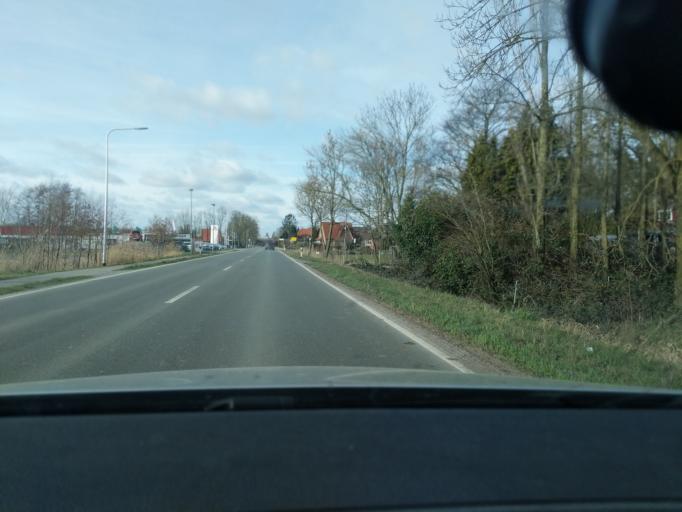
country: DE
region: Lower Saxony
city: Drochtersen
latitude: 53.7051
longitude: 9.3998
